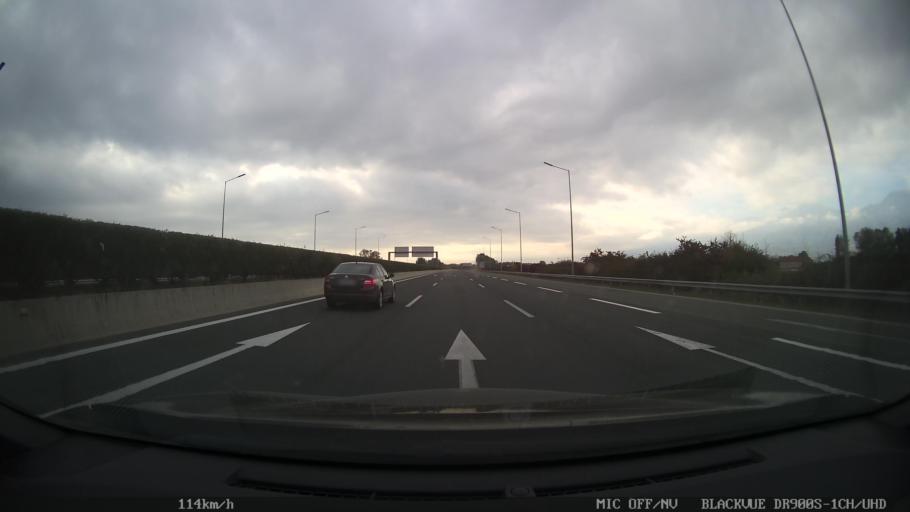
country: GR
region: Central Macedonia
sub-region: Nomos Pierias
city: Nea Efesos
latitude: 40.1914
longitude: 22.5497
